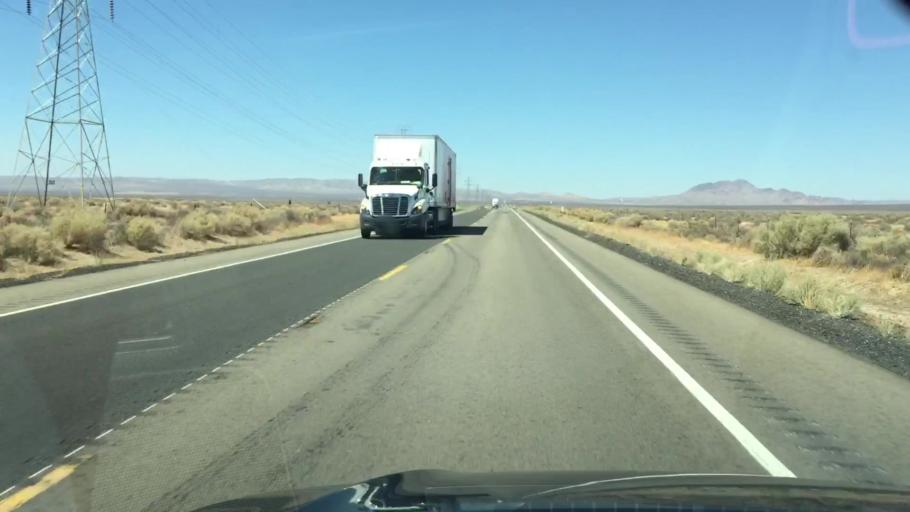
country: US
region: California
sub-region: Kern County
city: Boron
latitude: 35.1548
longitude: -117.5868
